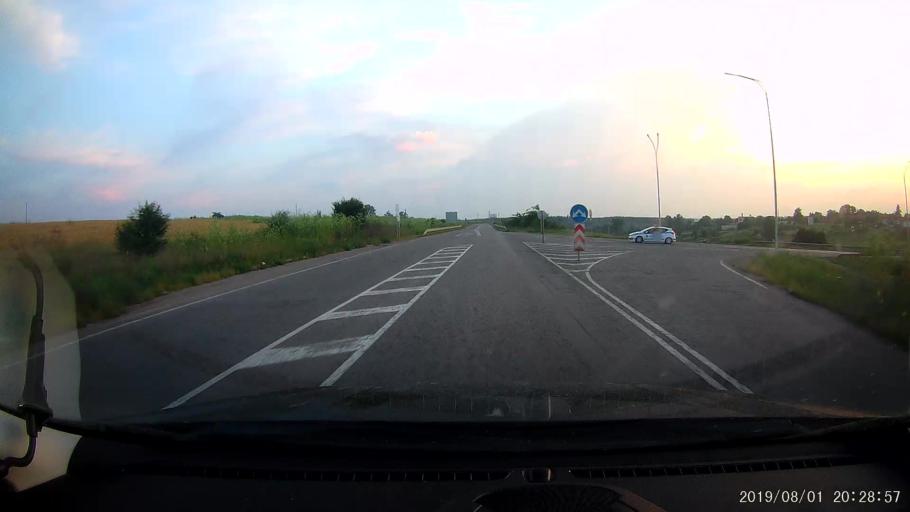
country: BG
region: Yambol
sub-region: Obshtina Elkhovo
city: Elkhovo
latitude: 42.1637
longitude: 26.5688
